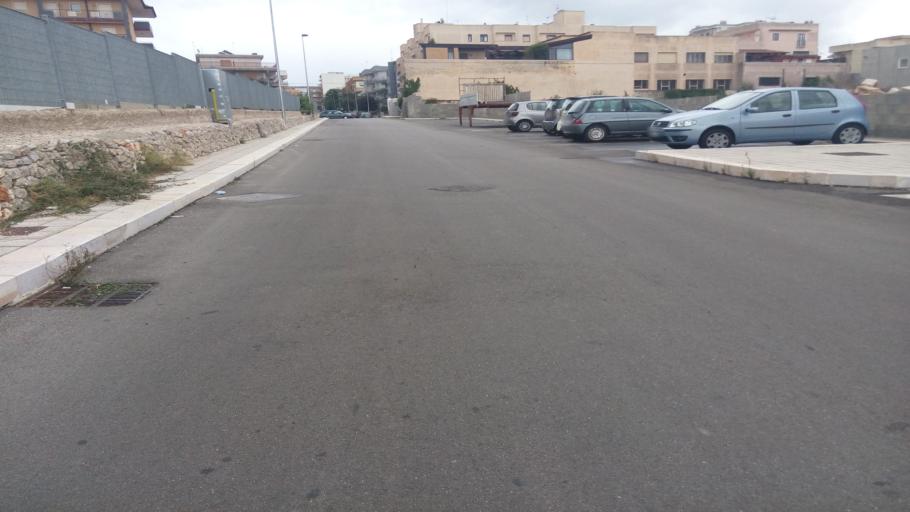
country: IT
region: Apulia
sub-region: Provincia di Bari
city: Putignano
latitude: 40.8562
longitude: 17.1145
